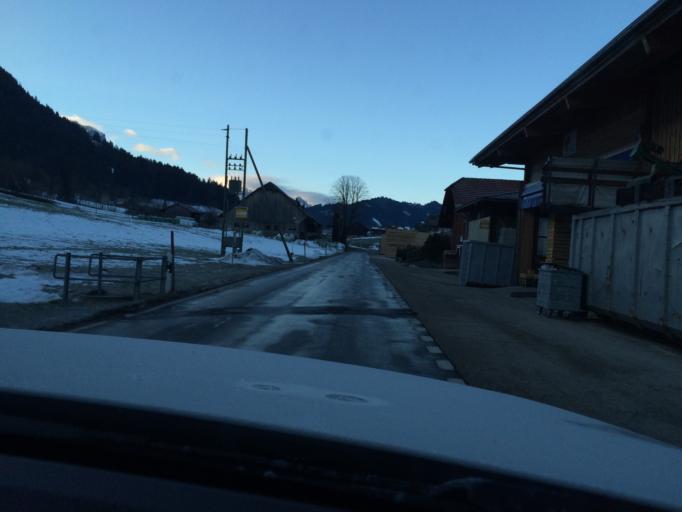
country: CH
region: Bern
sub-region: Emmental District
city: Wald
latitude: 46.8459
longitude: 7.8911
